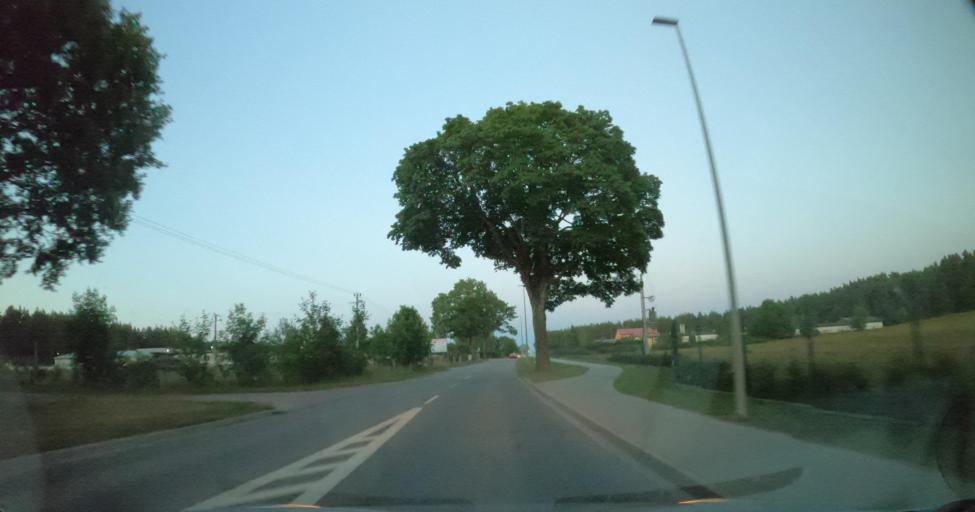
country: PL
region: Pomeranian Voivodeship
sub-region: Powiat wejherowski
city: Szemud
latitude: 54.4815
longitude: 18.2515
